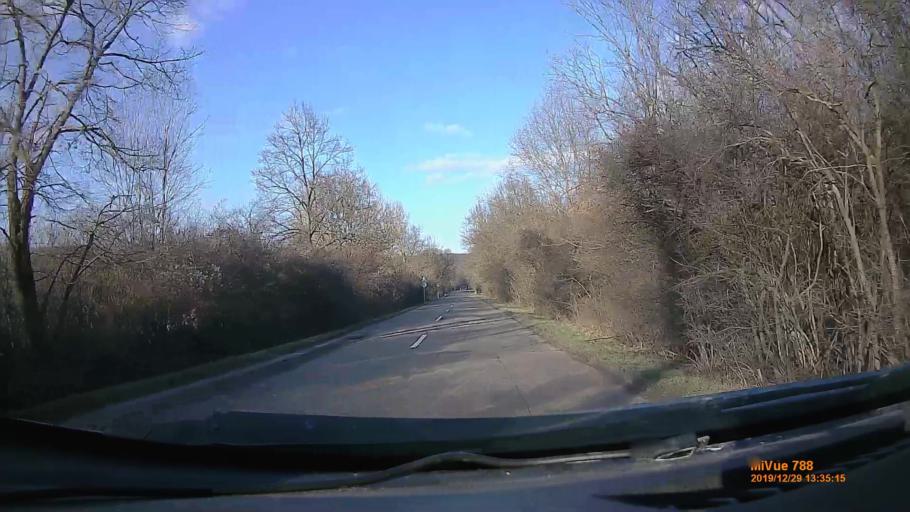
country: HU
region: Heves
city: Sirok
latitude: 47.9076
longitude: 20.1782
